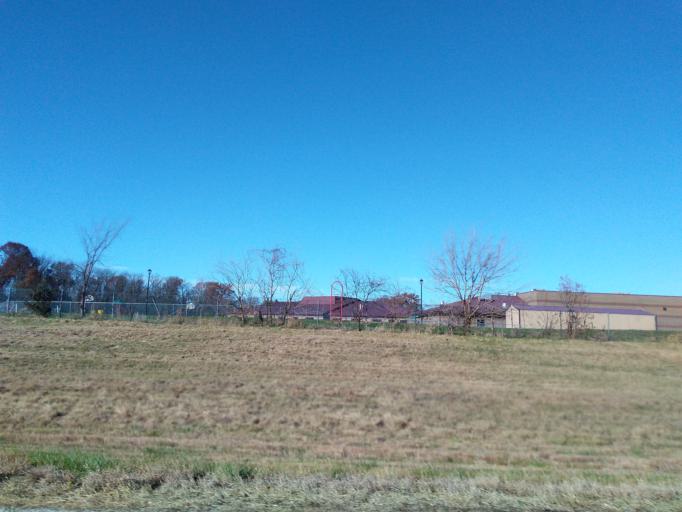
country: US
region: Illinois
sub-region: Saint Clair County
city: Dupo
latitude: 38.5133
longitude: -90.2019
